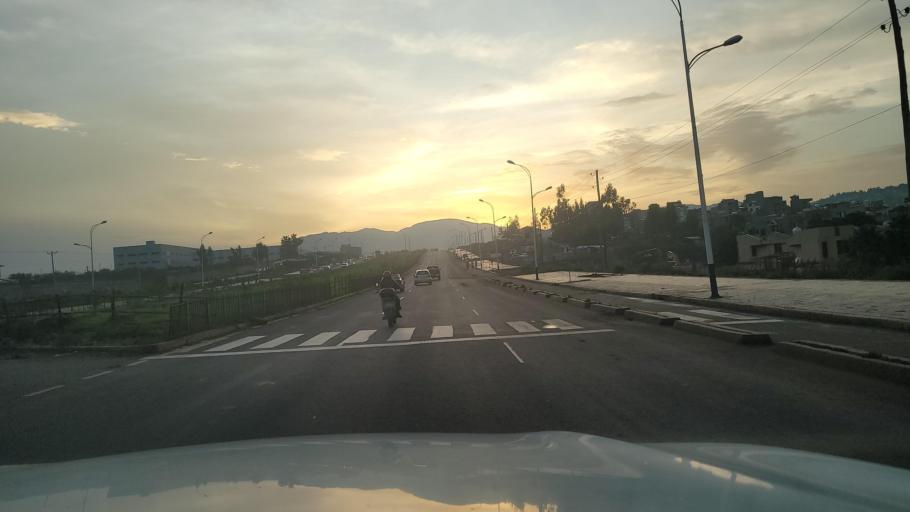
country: ET
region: Adis Abeba
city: Addis Ababa
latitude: 8.9497
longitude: 38.7097
